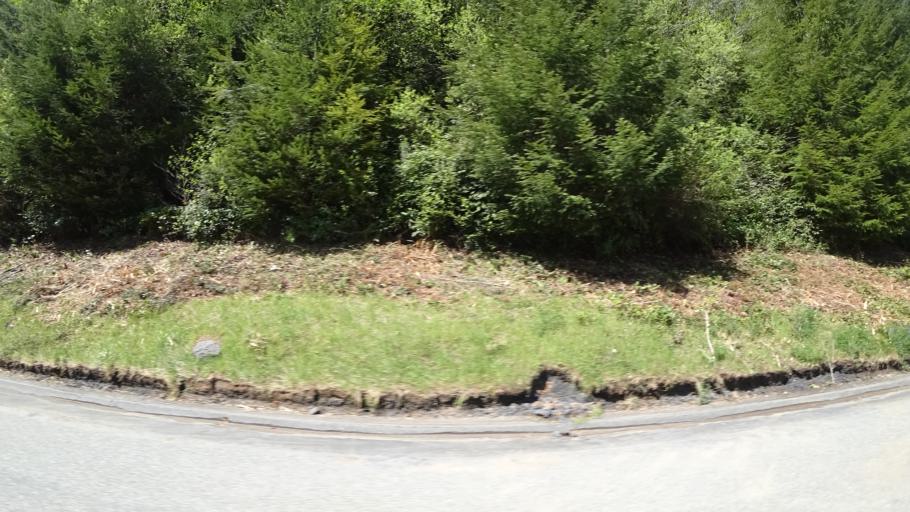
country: US
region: California
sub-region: Del Norte County
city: Bertsch-Oceanview
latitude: 41.4112
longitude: -124.0036
